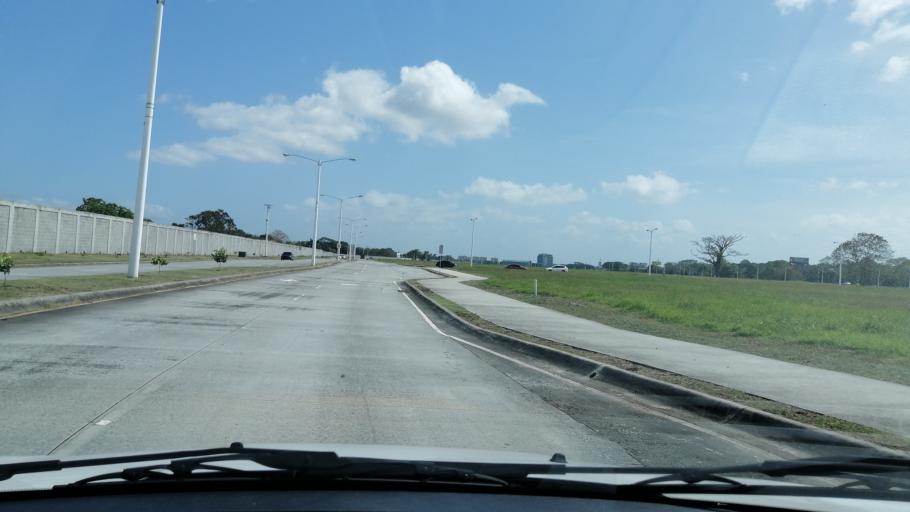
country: PA
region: Panama
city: San Miguelito
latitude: 9.0360
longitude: -79.4420
